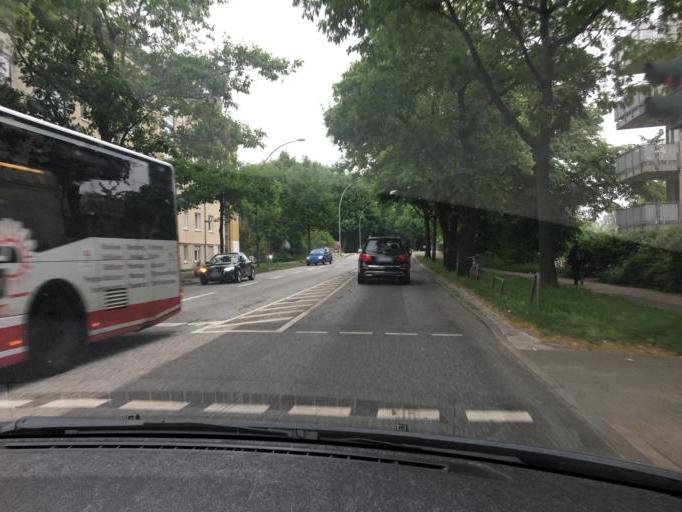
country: DE
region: Hamburg
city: Kleiner Grasbrook
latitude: 53.5162
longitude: 9.9934
